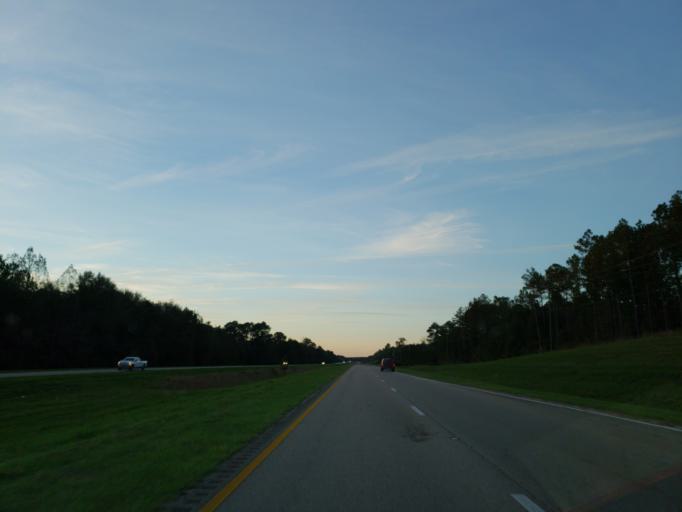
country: US
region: Mississippi
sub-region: Wayne County
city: Belmont
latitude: 31.5829
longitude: -88.5433
